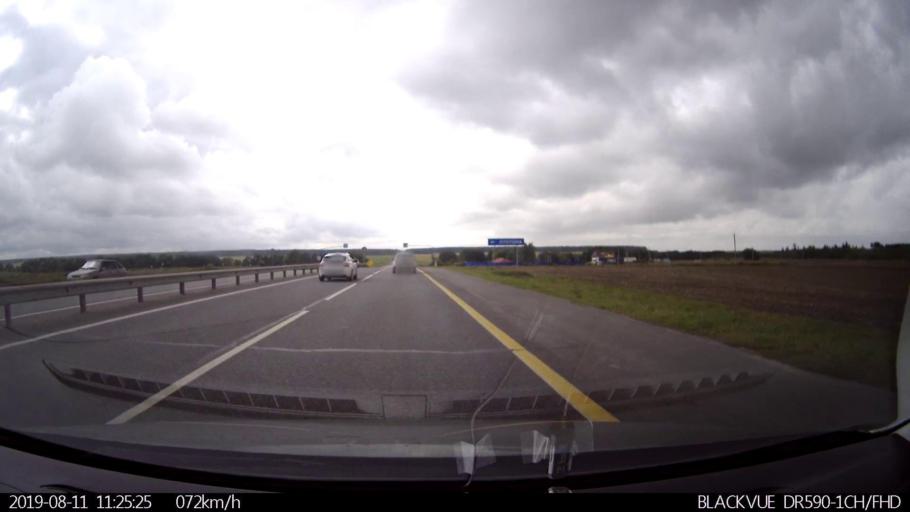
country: RU
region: Ulyanovsk
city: Krasnyy Gulyay
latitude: 54.1174
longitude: 48.2383
